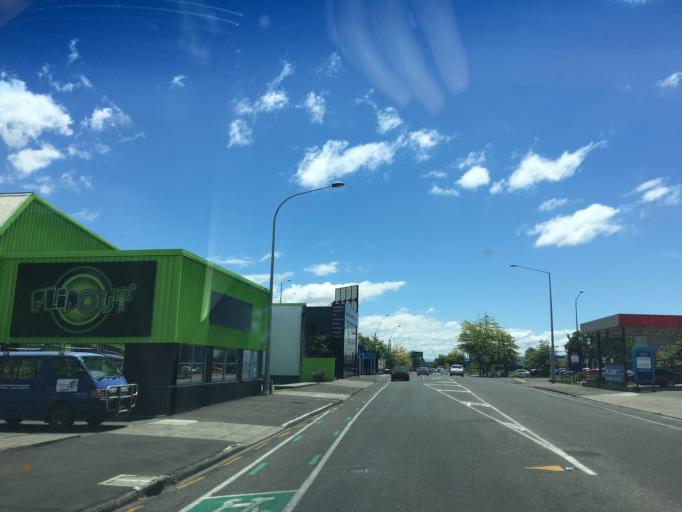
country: NZ
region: Hawke's Bay
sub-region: Hastings District
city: Hastings
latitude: -39.6432
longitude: 176.8500
